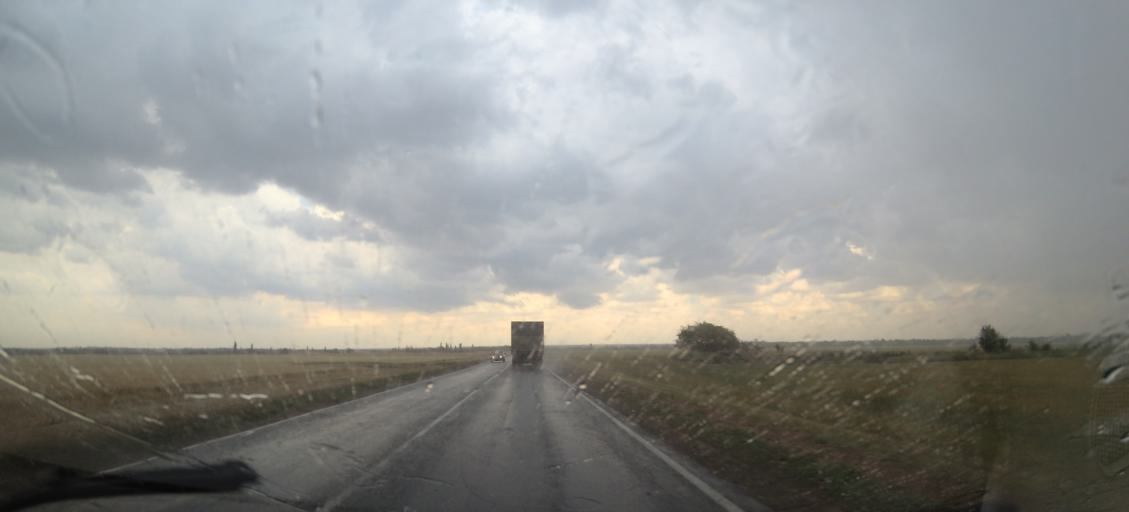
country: RU
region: Rostov
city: Orlovskiy
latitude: 46.8671
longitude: 41.9682
